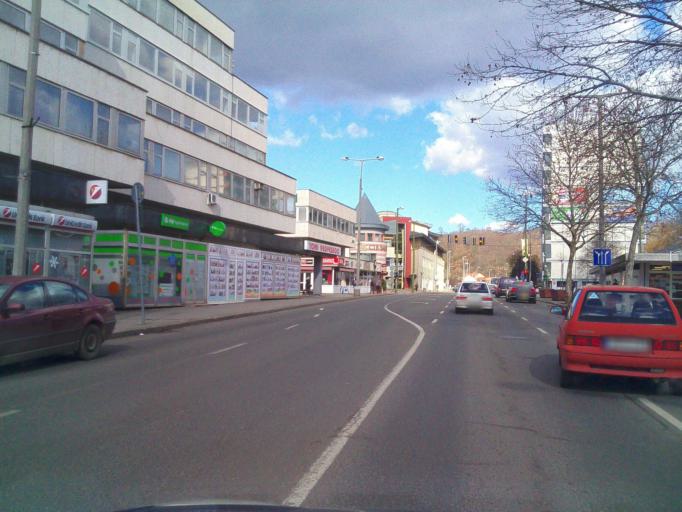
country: HU
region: Nograd
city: Salgotarjan
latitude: 48.1063
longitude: 19.8093
